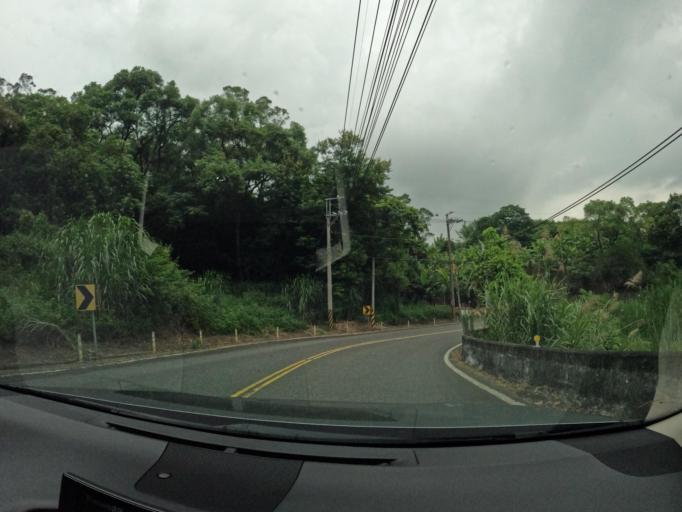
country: TW
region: Taiwan
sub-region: Nantou
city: Nantou
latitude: 23.8665
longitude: 120.7686
